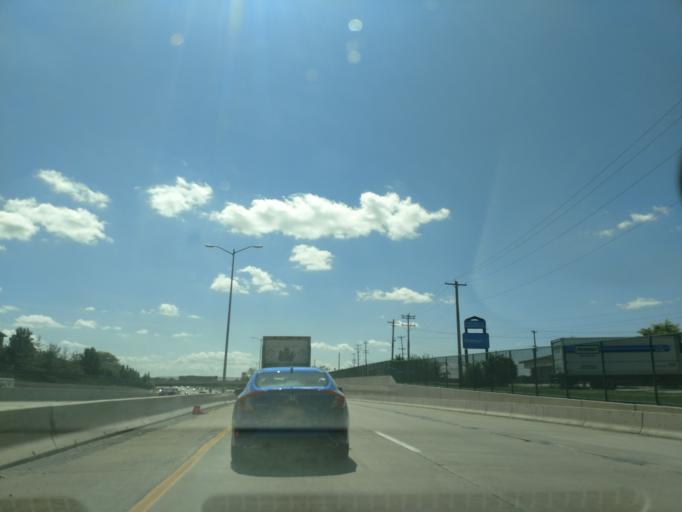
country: US
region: Pennsylvania
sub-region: Montgomery County
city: King of Prussia
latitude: 40.0825
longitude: -75.3993
